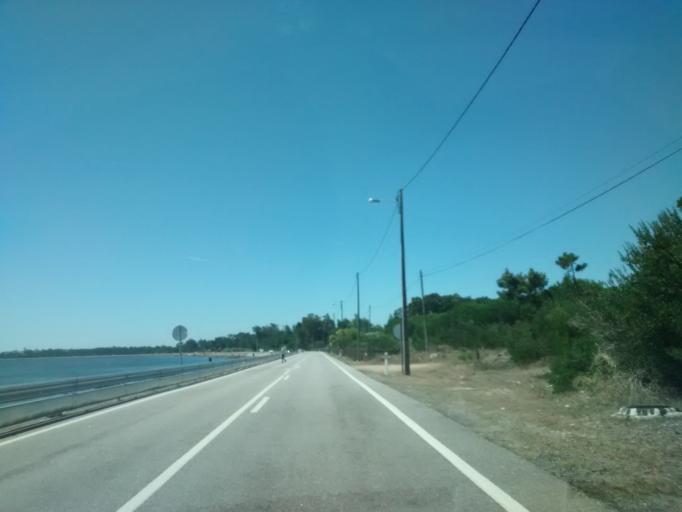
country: PT
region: Aveiro
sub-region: Ilhavo
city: Gafanha da Nazare
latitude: 40.7074
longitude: -8.7126
